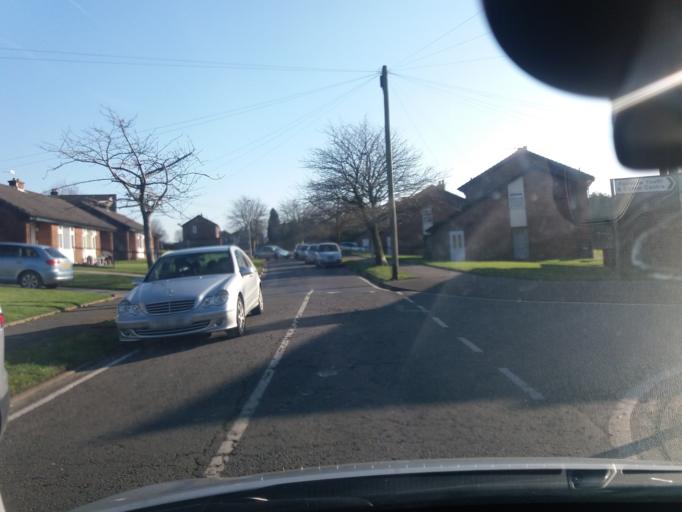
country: GB
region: England
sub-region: Lancashire
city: Adlington
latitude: 53.6179
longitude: -2.6054
